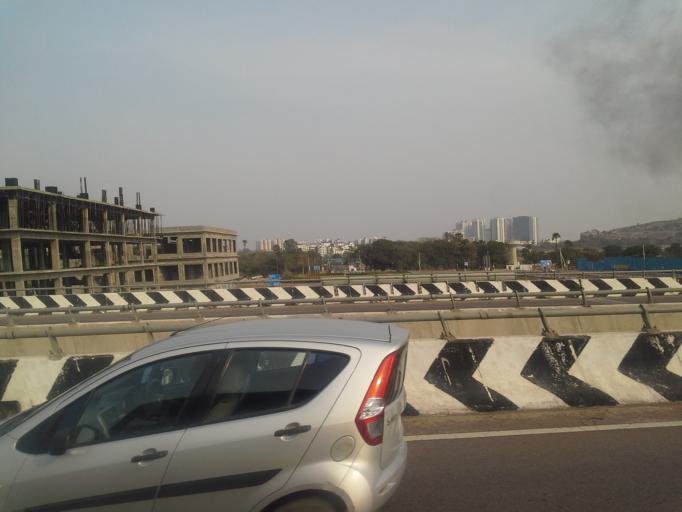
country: IN
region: Telangana
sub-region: Rangareddi
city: Kukatpalli
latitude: 17.4190
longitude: 78.3562
